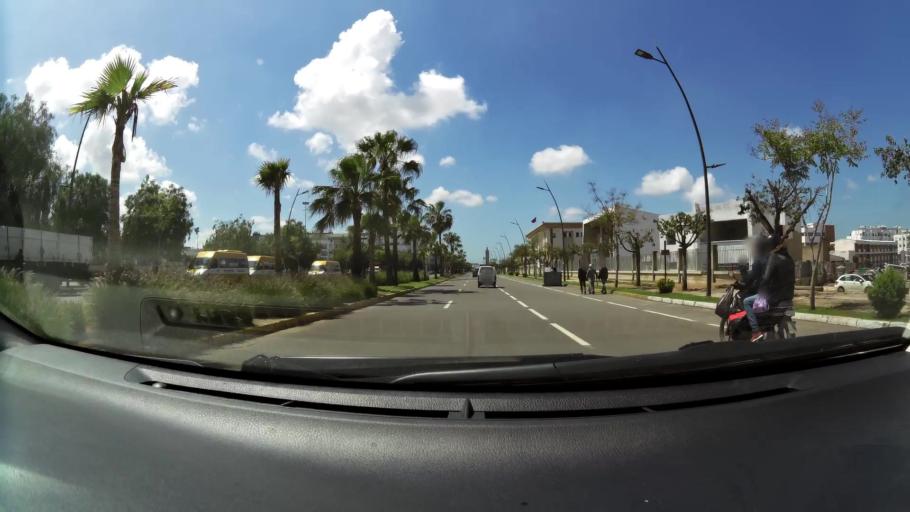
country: MA
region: Grand Casablanca
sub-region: Casablanca
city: Casablanca
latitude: 33.5569
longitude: -7.5823
